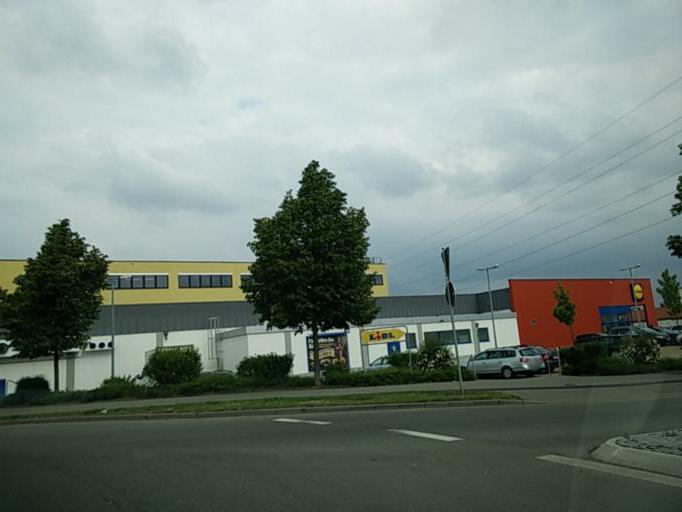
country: DE
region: Baden-Wuerttemberg
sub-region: Regierungsbezirk Stuttgart
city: Holzgerlingen
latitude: 48.6465
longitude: 9.0070
